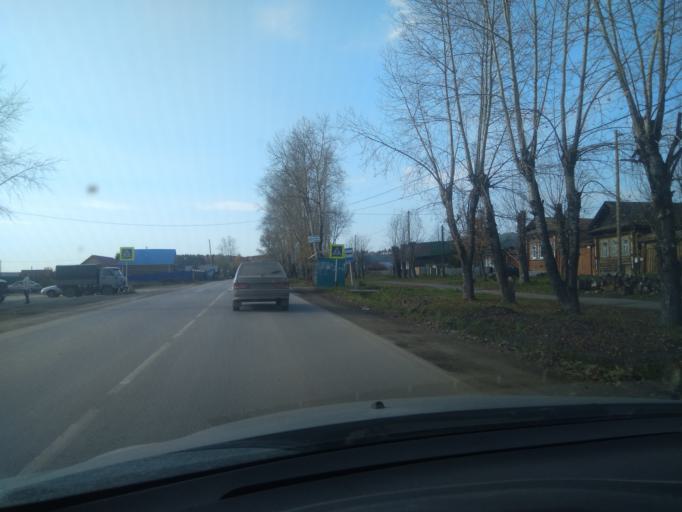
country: RU
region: Sverdlovsk
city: Nizhniye Sergi
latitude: 56.6574
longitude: 59.2991
